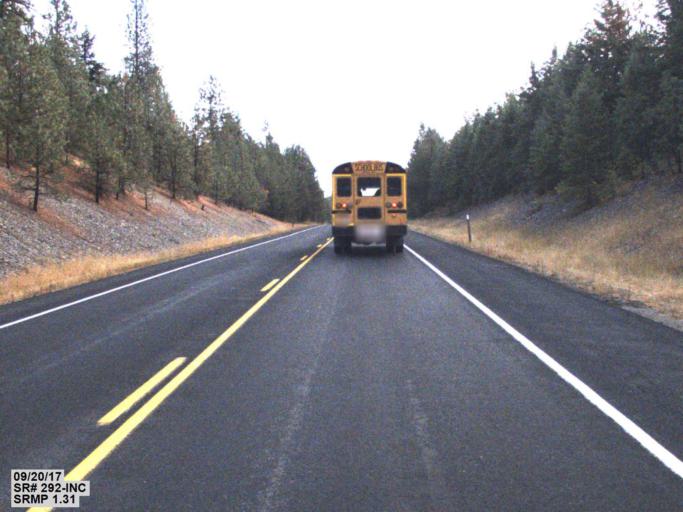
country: US
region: Washington
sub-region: Stevens County
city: Chewelah
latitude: 48.0644
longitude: -117.7156
